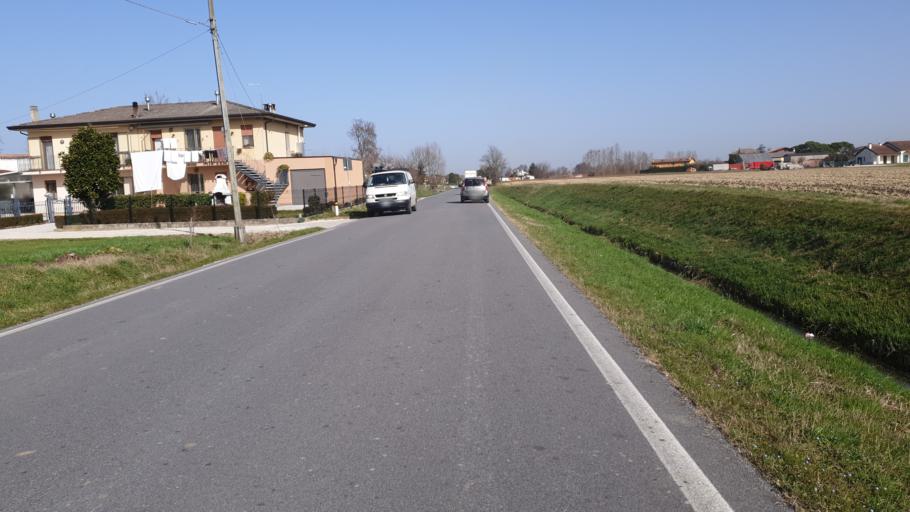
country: IT
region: Veneto
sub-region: Provincia di Padova
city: Cavino
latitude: 45.5092
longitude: 11.8906
